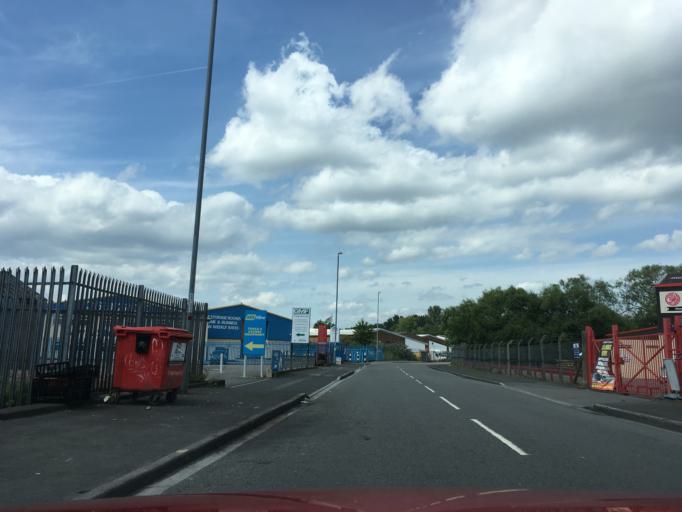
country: GB
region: Wales
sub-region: Newport
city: Nash
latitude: 51.5725
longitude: -2.9478
